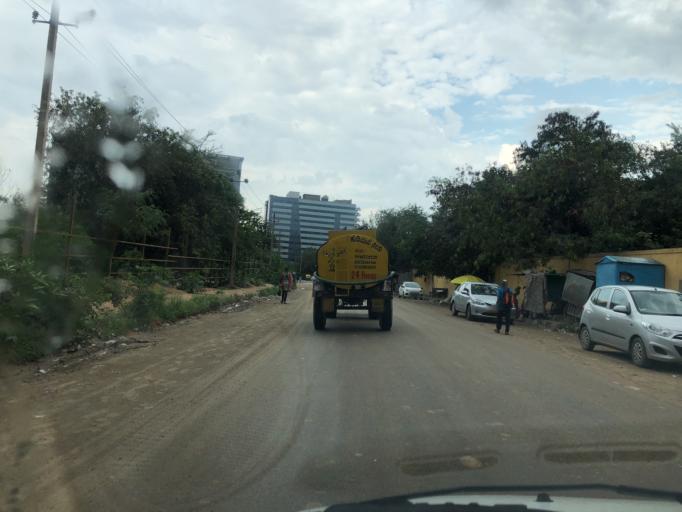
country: IN
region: Karnataka
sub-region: Bangalore Urban
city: Bangalore
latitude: 12.9824
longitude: 77.6957
